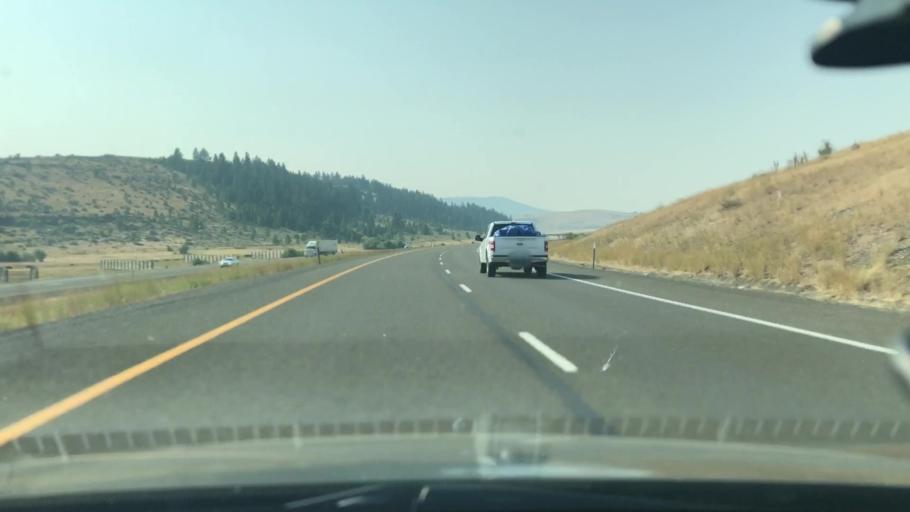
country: US
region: Oregon
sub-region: Union County
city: Union
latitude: 45.1747
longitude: -117.9777
